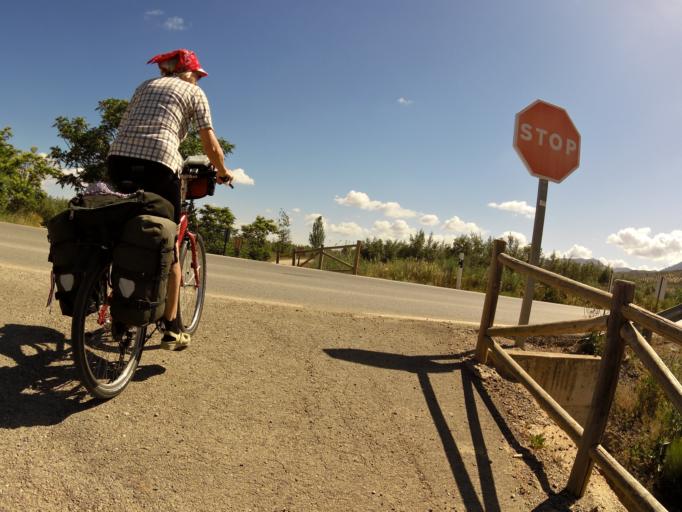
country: ES
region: Andalusia
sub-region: Provincia de Jaen
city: Alcaudete
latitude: 37.6071
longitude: -4.1284
